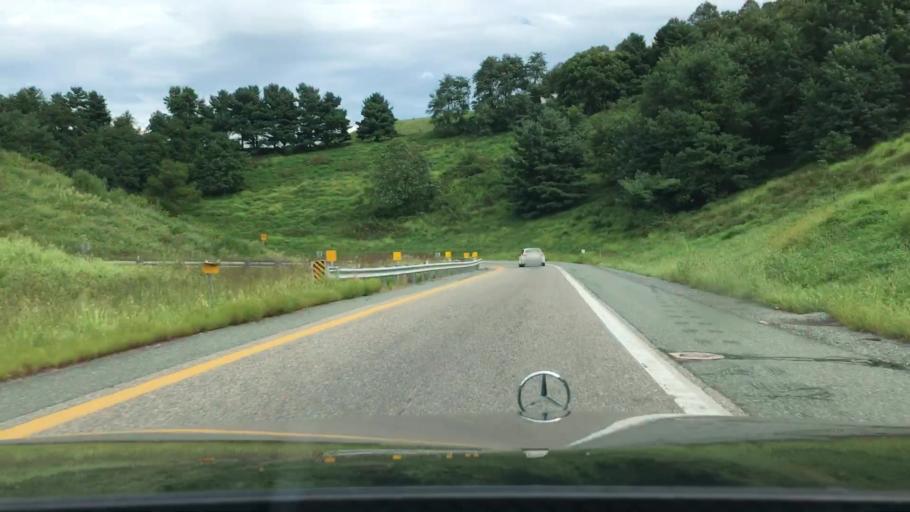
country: US
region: Virginia
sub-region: City of Waynesboro
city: Waynesboro
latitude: 38.0321
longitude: -78.8636
